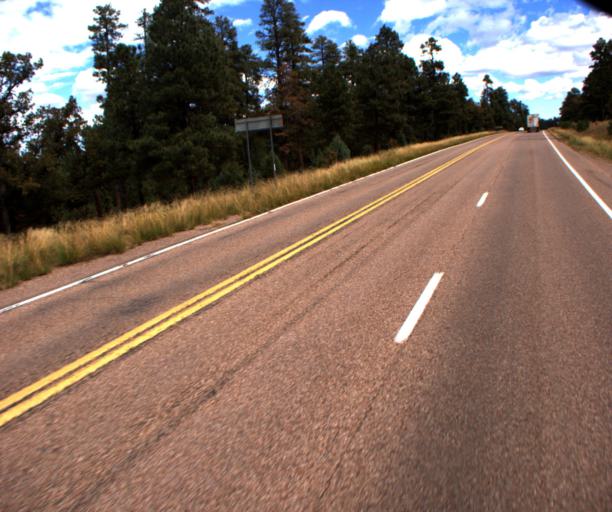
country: US
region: Arizona
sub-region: Navajo County
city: Heber-Overgaard
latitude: 34.3672
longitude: -110.6873
